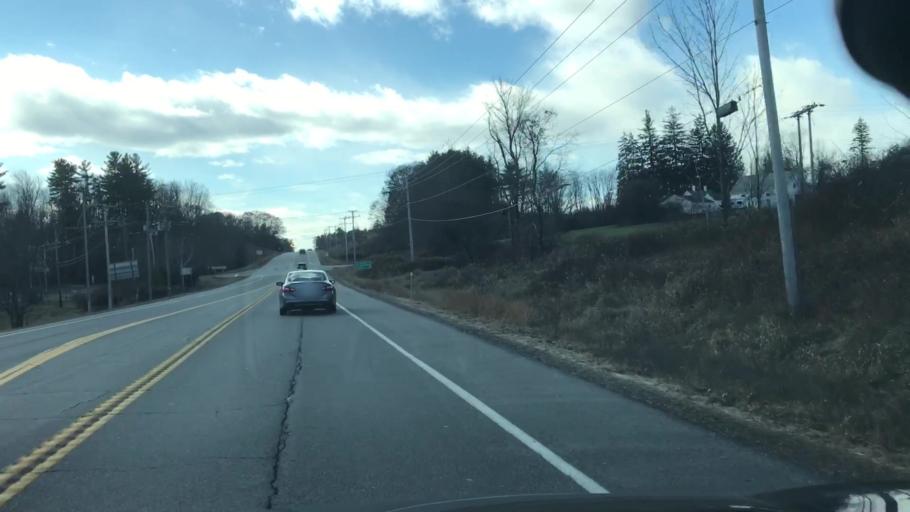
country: US
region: New Hampshire
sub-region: Merrimack County
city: Pittsfield
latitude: 43.3074
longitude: -71.3366
